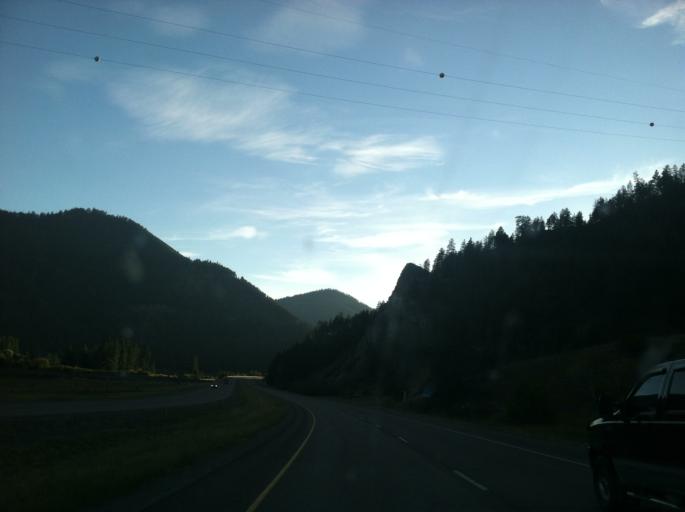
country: US
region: Montana
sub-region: Missoula County
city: Clinton
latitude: 46.7029
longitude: -113.4725
